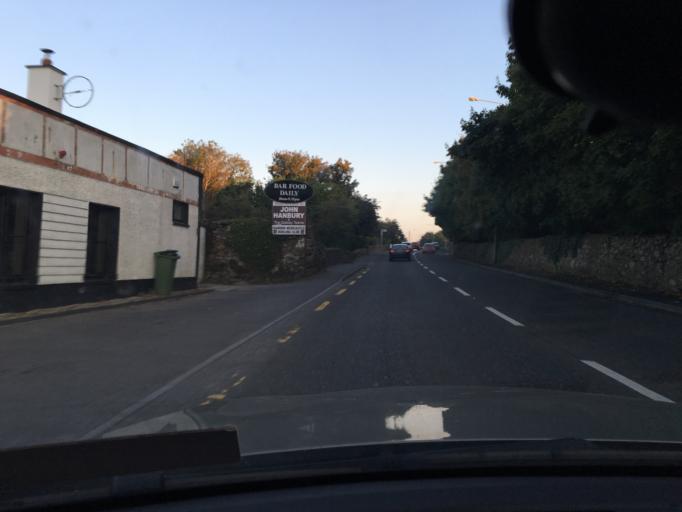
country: IE
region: Connaught
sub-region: County Galway
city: Gaillimh
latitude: 53.2965
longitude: -9.0935
